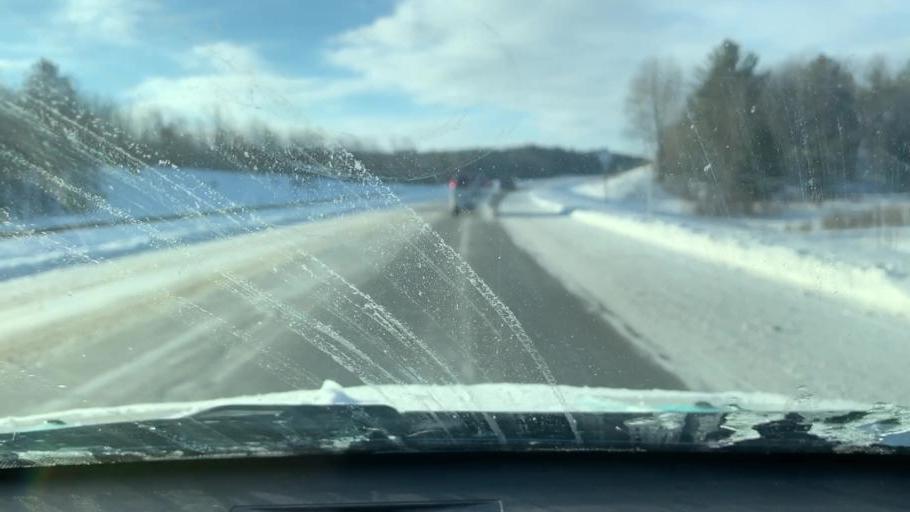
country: US
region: Michigan
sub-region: Wexford County
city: Cadillac
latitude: 44.2427
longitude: -85.3683
